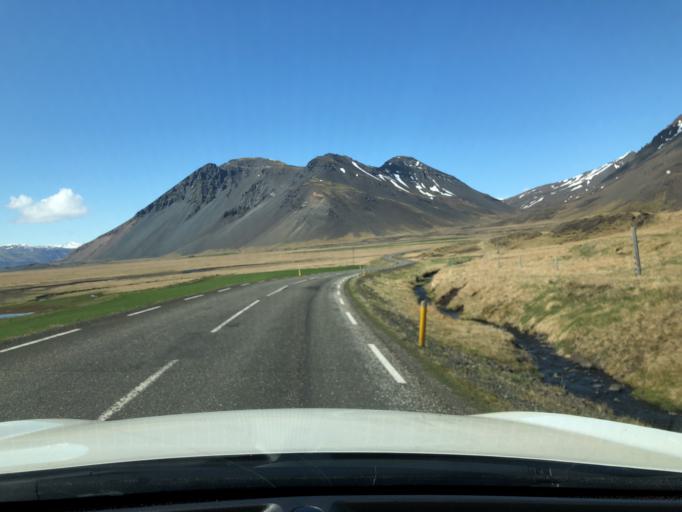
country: IS
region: East
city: Hoefn
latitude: 64.4283
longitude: -14.6270
